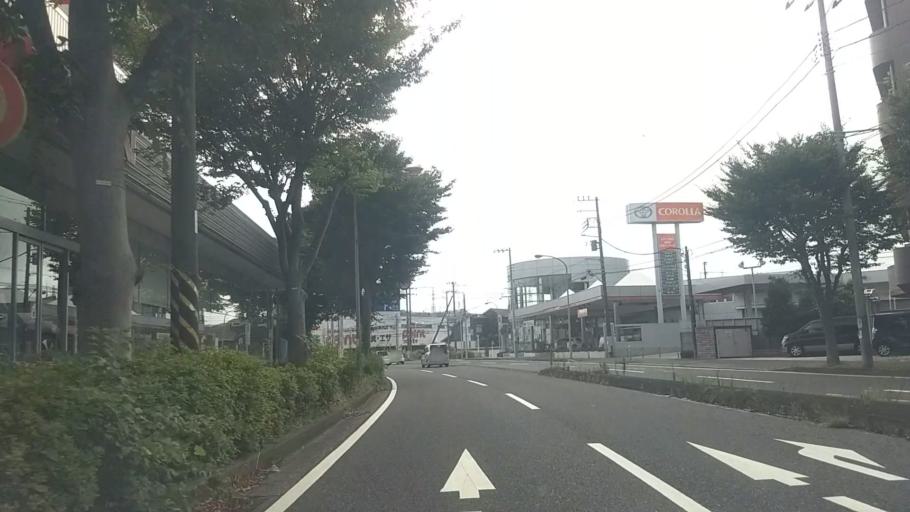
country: JP
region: Kanagawa
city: Yokosuka
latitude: 35.2435
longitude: 139.6815
